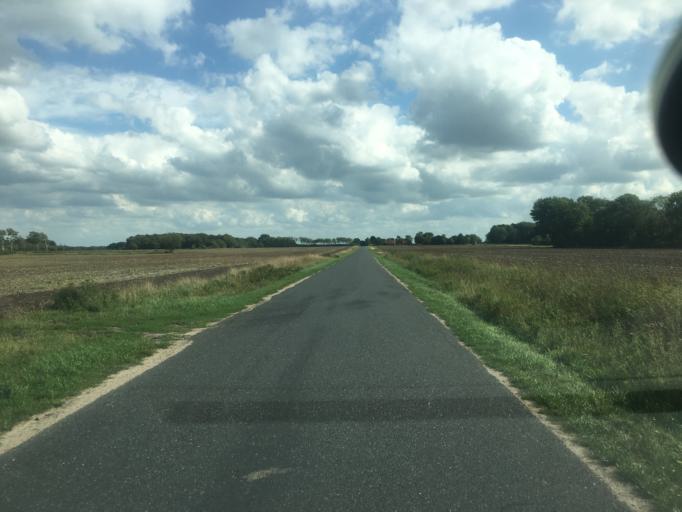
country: DK
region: South Denmark
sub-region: Tonder Kommune
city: Logumkloster
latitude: 55.0192
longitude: 8.9916
